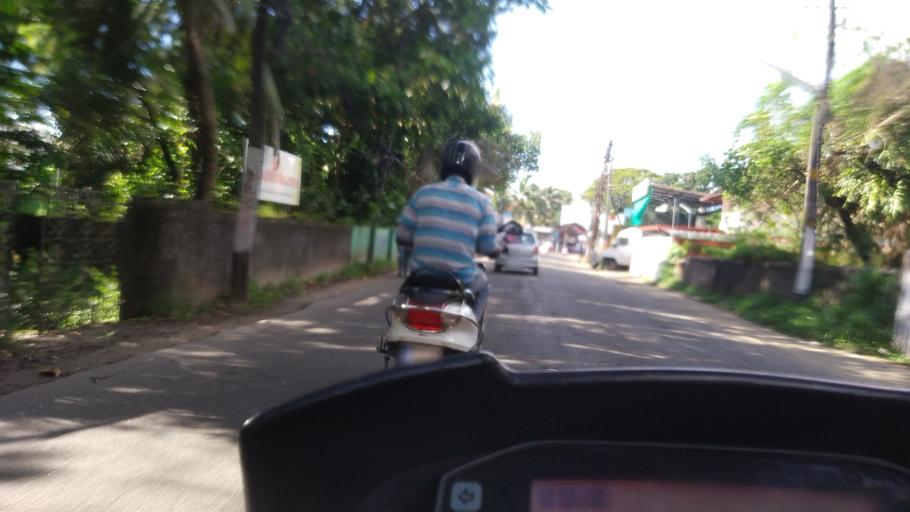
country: IN
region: Kerala
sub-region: Ernakulam
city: Elur
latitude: 10.0586
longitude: 76.2143
